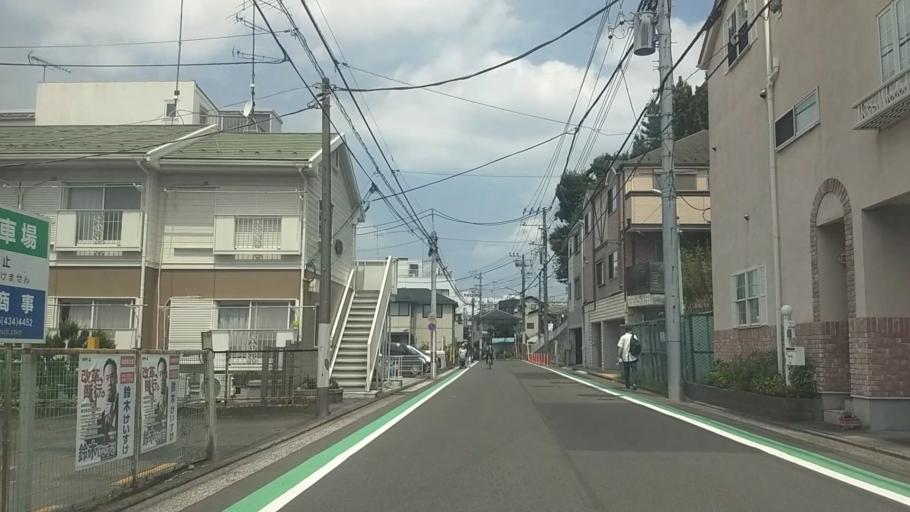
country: JP
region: Kanagawa
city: Yokohama
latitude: 35.5057
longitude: 139.6350
